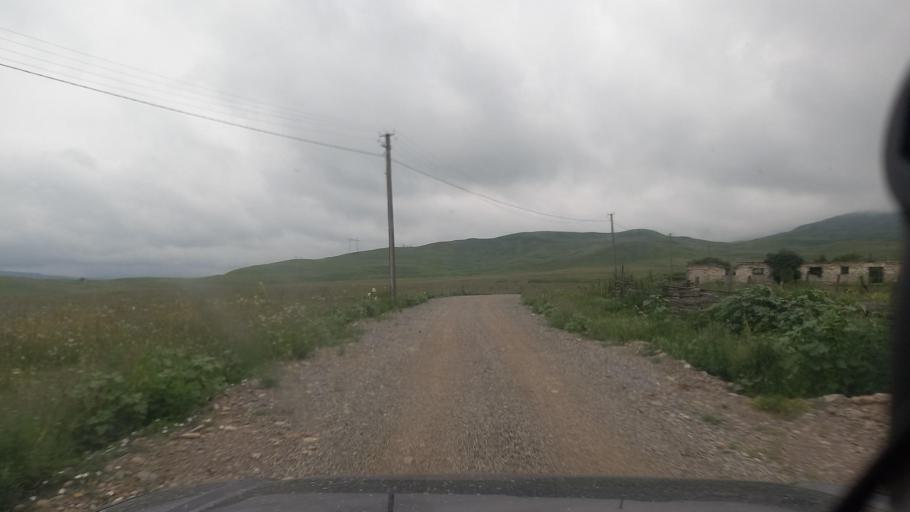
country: RU
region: Karachayevo-Cherkesiya
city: Pregradnaya
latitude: 43.9973
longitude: 41.1904
